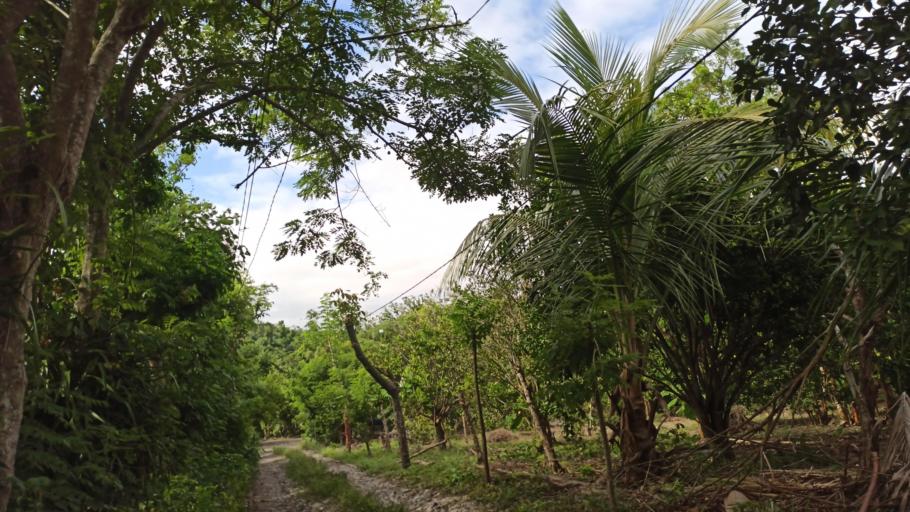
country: MX
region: Veracruz
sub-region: Papantla
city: Residencial Tajin
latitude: 20.6430
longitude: -97.3618
